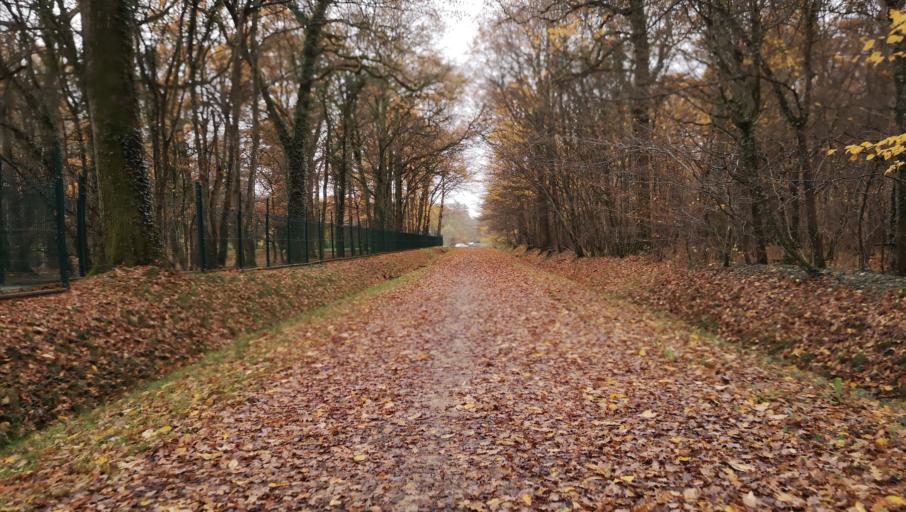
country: FR
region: Centre
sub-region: Departement du Loiret
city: Saint-Jean-de-Braye
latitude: 47.9274
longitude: 1.9857
